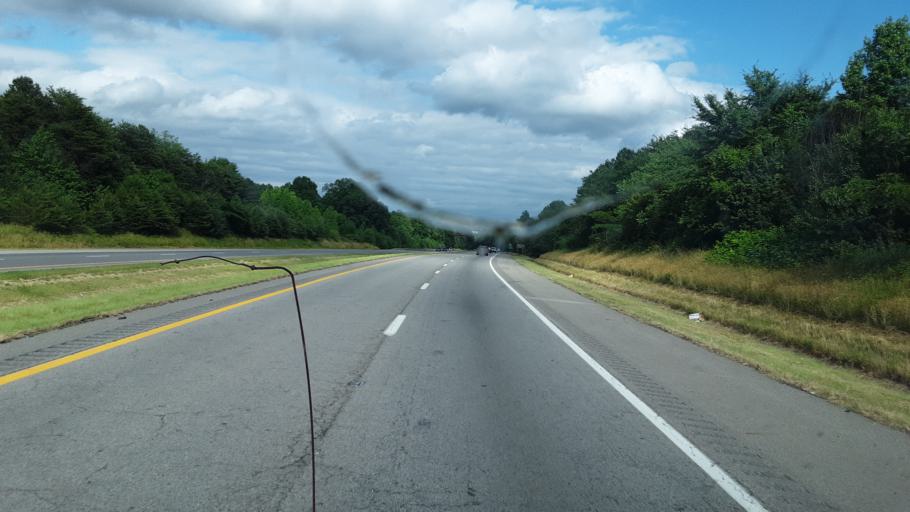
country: US
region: Virginia
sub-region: City of Danville
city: Danville
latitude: 36.5463
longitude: -79.4293
